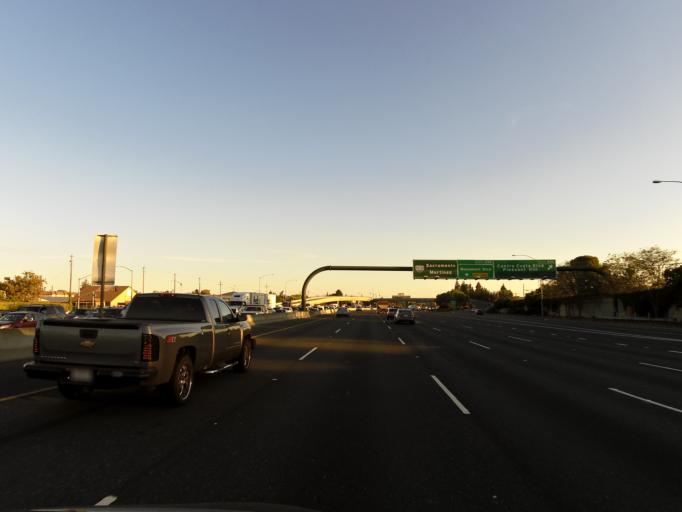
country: US
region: California
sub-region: Contra Costa County
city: Pleasant Hill
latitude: 37.9369
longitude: -122.0602
